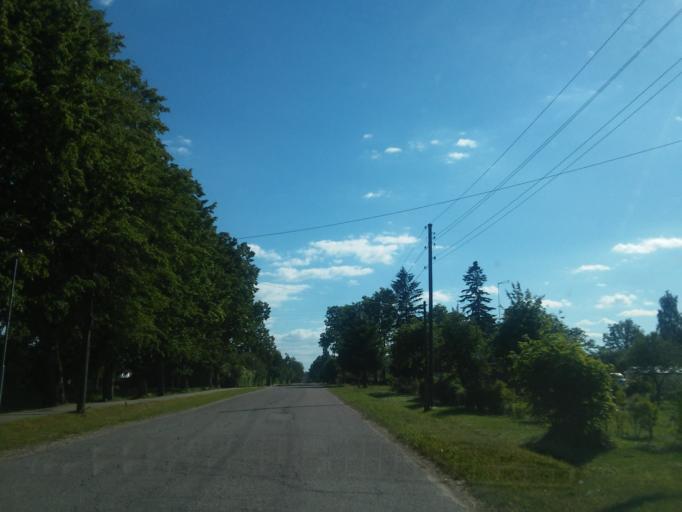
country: LV
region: Vainode
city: Vainode
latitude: 56.4239
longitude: 21.8627
